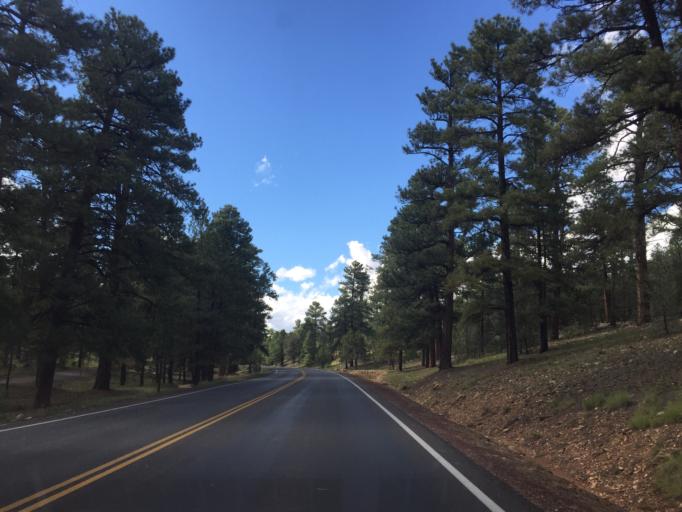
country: US
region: Arizona
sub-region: Coconino County
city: Grand Canyon
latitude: 36.0544
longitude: -112.1272
